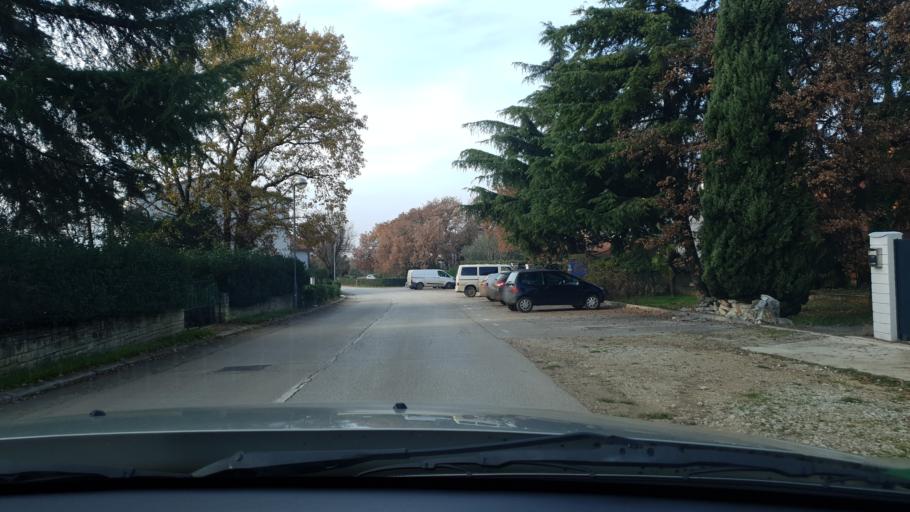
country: HR
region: Istarska
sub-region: Grad Porec
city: Porec
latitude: 45.2503
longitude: 13.6143
